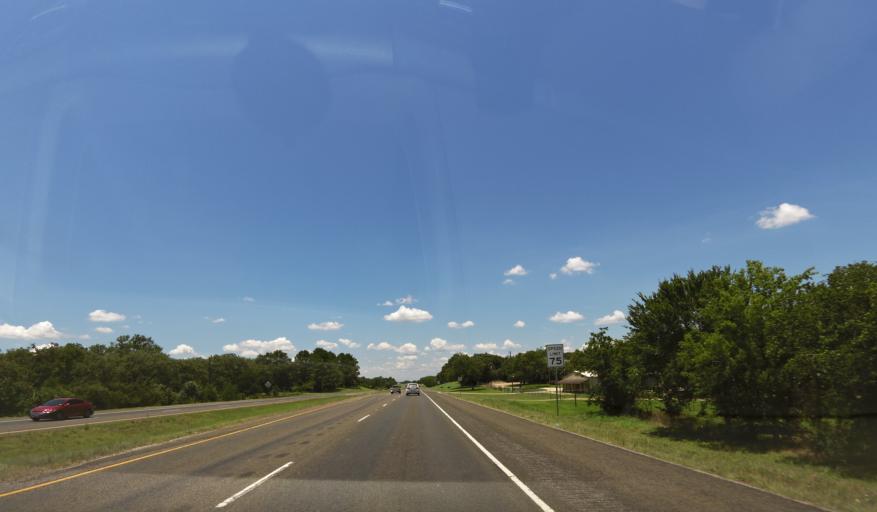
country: US
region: Texas
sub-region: Washington County
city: Brenham
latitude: 30.1808
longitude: -96.4760
